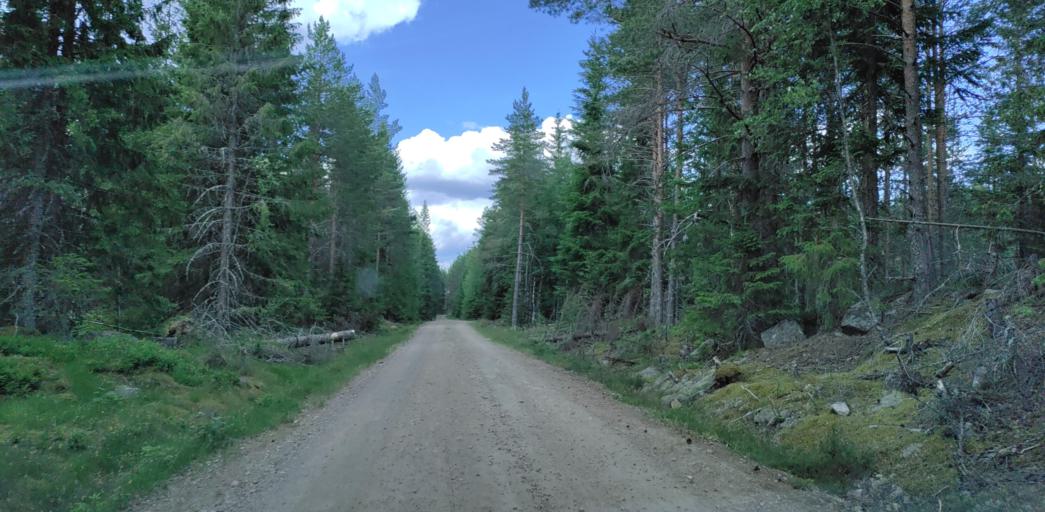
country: SE
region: Vaermland
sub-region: Hagfors Kommun
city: Ekshaerad
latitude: 60.0810
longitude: 13.3461
